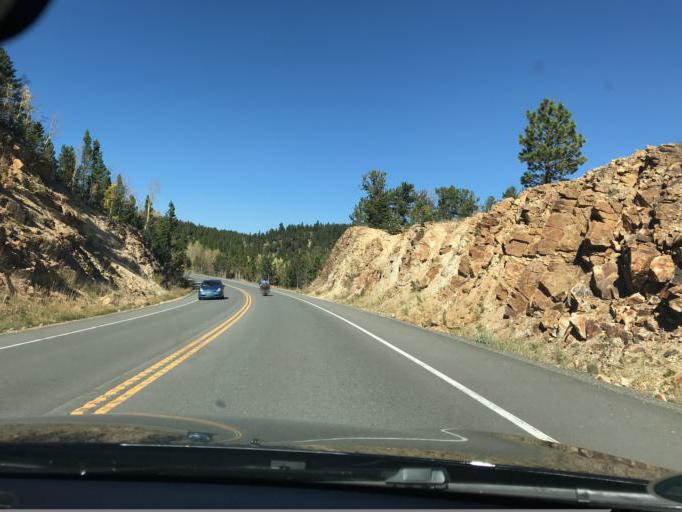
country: US
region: Colorado
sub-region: Boulder County
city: Nederland
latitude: 40.0633
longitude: -105.5160
